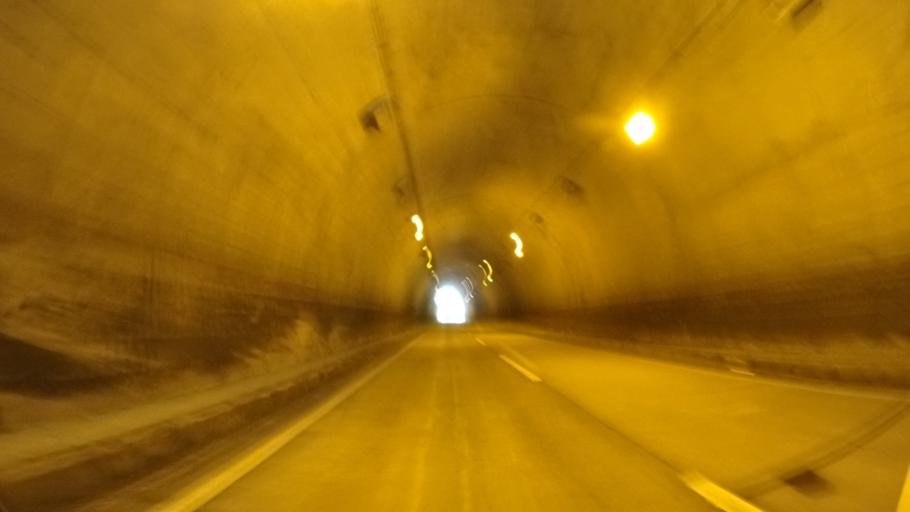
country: JP
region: Kagoshima
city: Kokubu-matsuki
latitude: 31.8283
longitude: 130.7317
